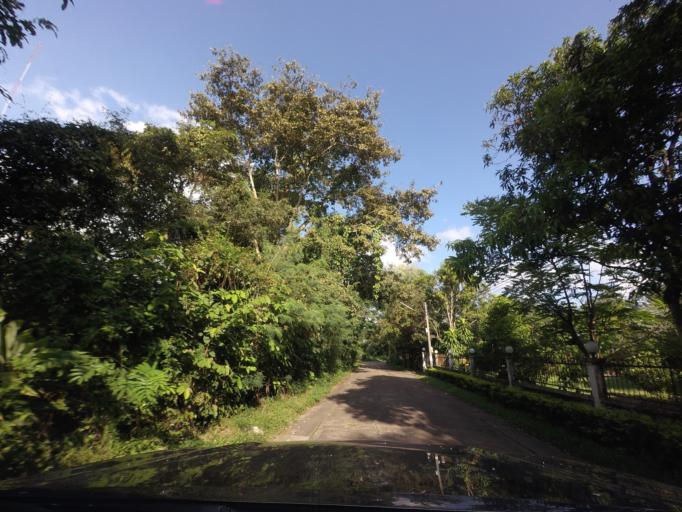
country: TH
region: Nong Khai
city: Nong Khai
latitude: 17.8859
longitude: 102.7732
